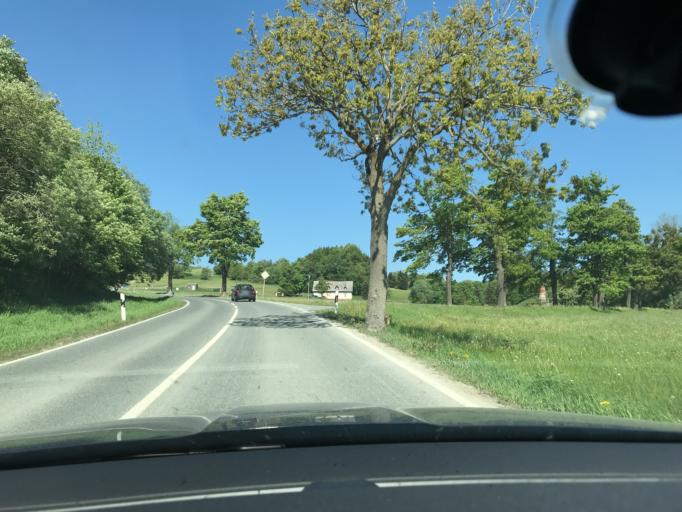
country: CZ
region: Ustecky
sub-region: Okres Chomutov
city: Kovarska
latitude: 50.4474
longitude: 13.0116
